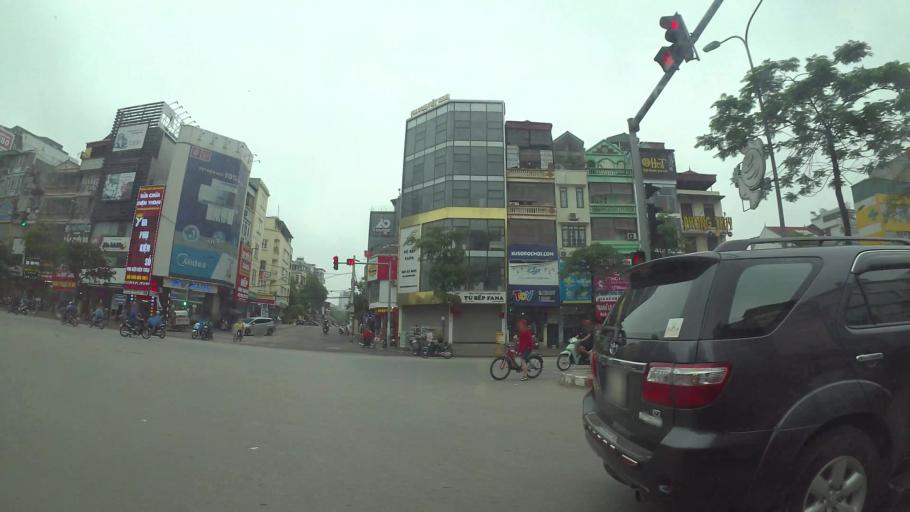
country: VN
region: Ha Noi
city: Dong Da
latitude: 21.0141
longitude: 105.8342
